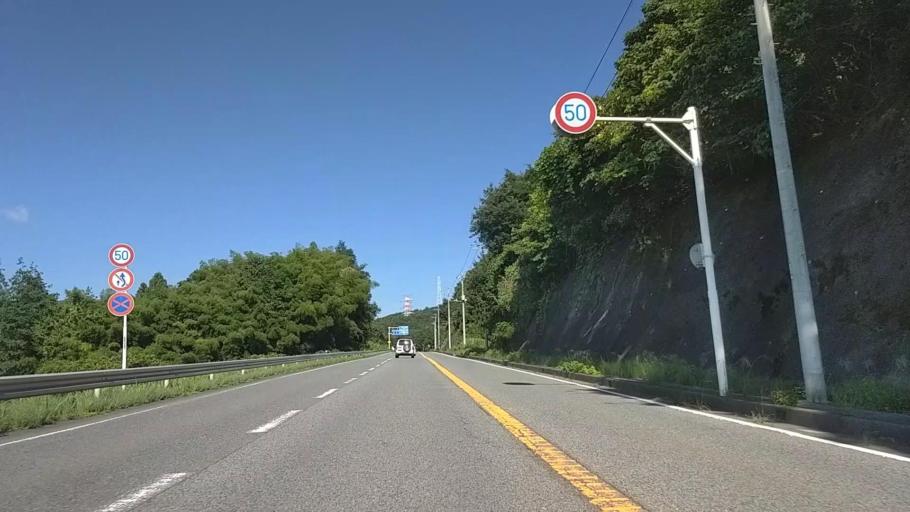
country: JP
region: Gunma
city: Annaka
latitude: 36.3190
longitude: 138.7940
